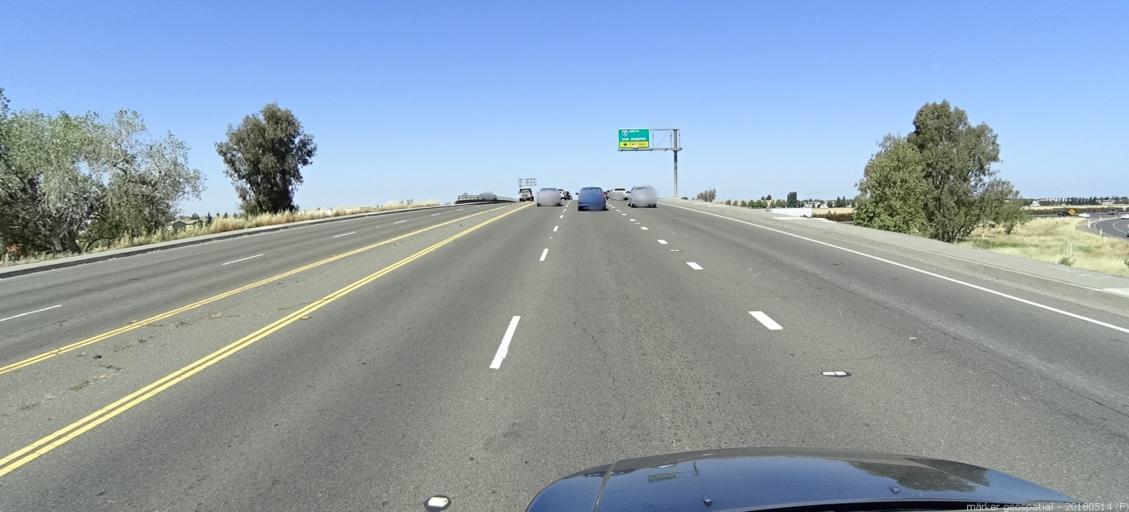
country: US
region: California
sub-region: Yolo County
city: West Sacramento
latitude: 38.6559
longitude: -121.5317
